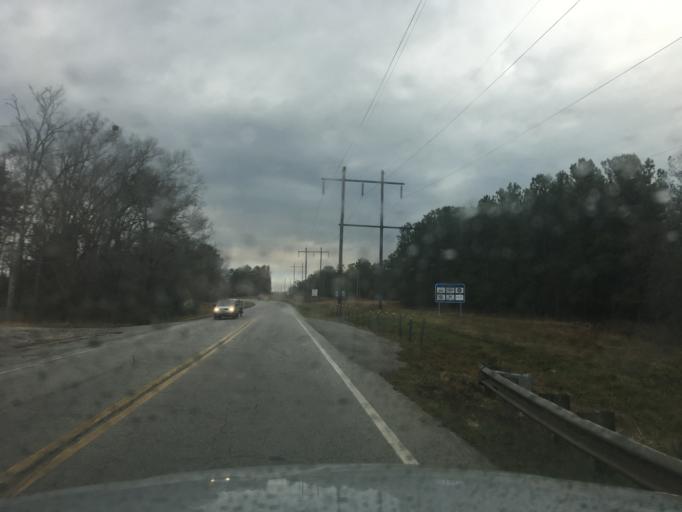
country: US
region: Georgia
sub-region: Columbia County
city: Appling
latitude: 33.7033
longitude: -82.3445
